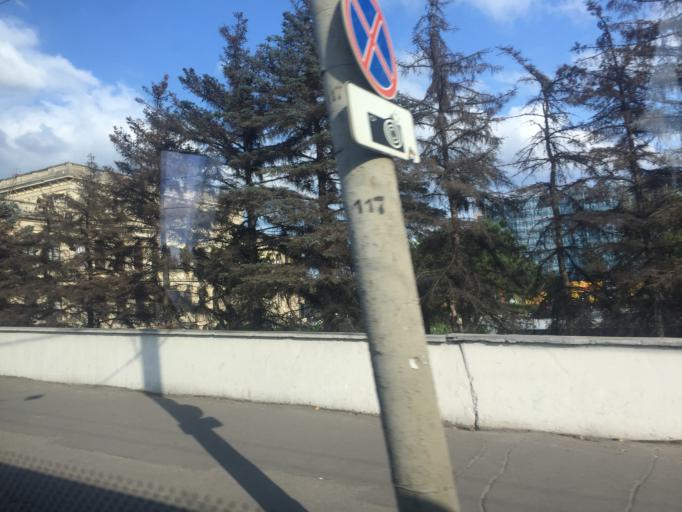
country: RU
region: Kaliningrad
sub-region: Gorod Kaliningrad
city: Kaliningrad
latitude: 54.7045
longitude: 20.5062
